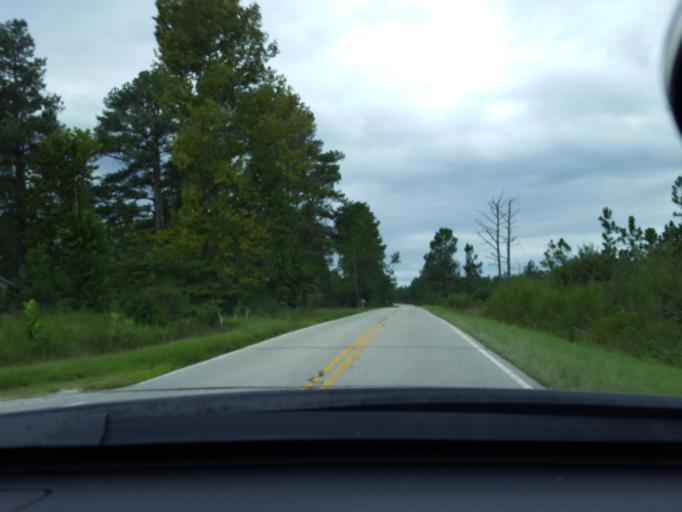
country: US
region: North Carolina
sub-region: Sampson County
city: Clinton
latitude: 34.8005
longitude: -78.2604
